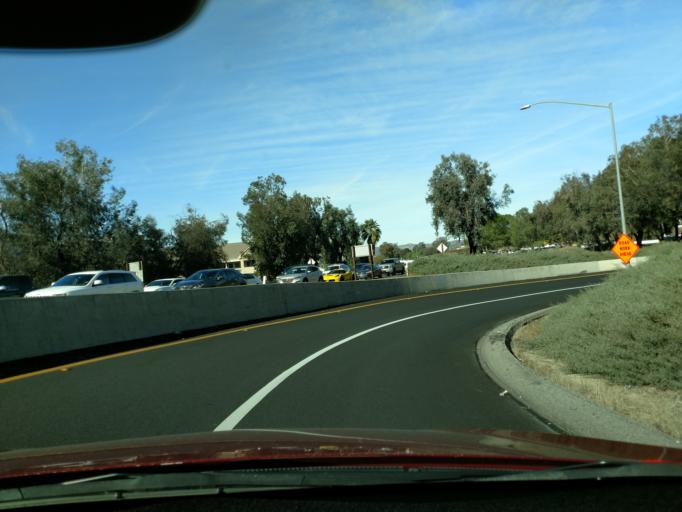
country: US
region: California
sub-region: Riverside County
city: Temecula
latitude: 33.5222
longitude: -117.1642
